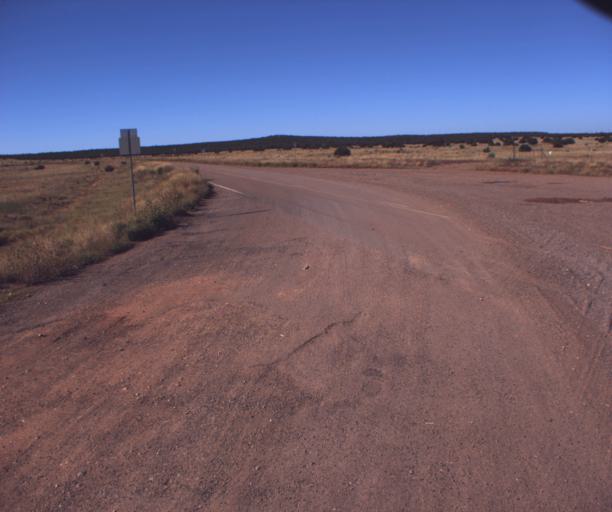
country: US
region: Arizona
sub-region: Navajo County
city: Heber-Overgaard
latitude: 34.4970
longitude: -110.3387
